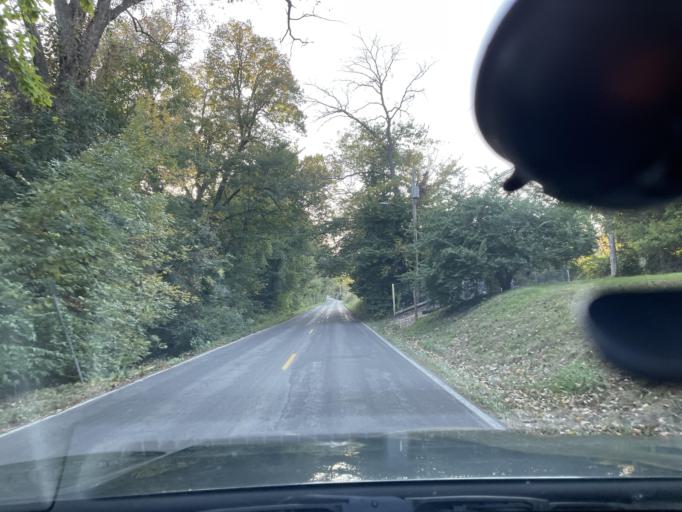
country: US
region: Missouri
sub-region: Andrew County
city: Country Club Village
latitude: 39.7994
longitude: -94.8304
